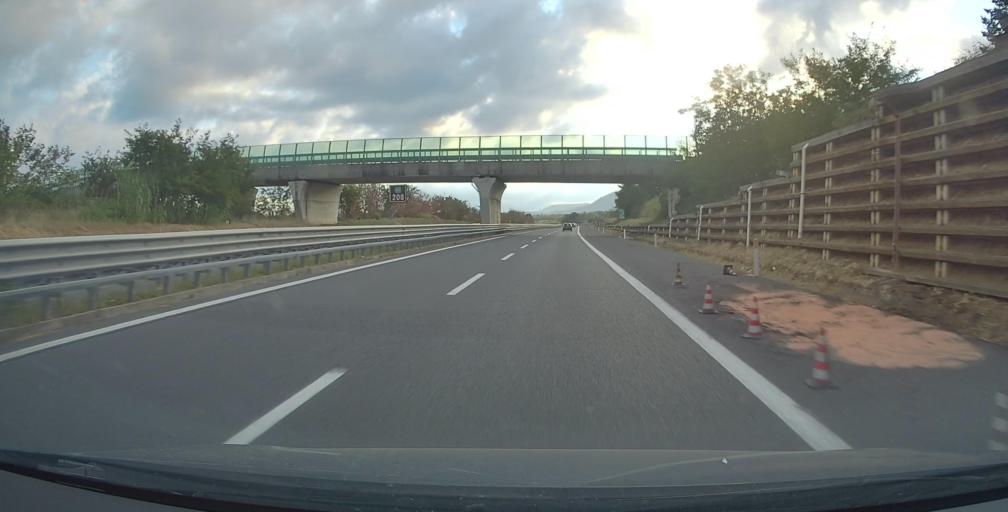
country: IT
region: Calabria
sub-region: Provincia di Catanzaro
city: Acconia
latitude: 38.8214
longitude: 16.2429
